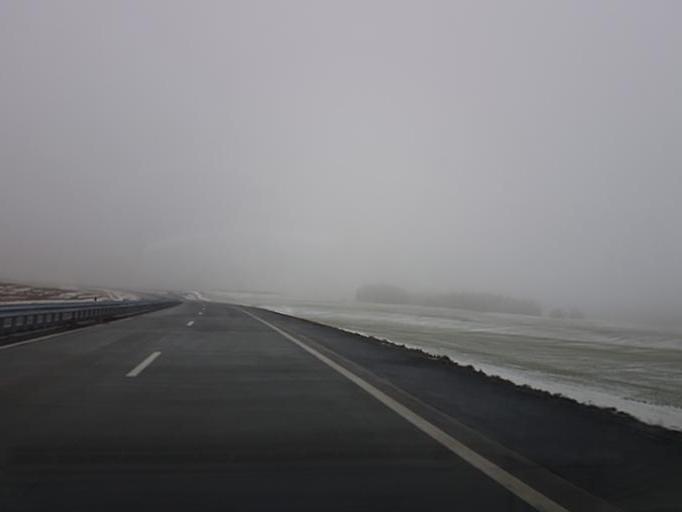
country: BY
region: Minsk
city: Atolina
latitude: 53.7537
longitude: 27.4107
